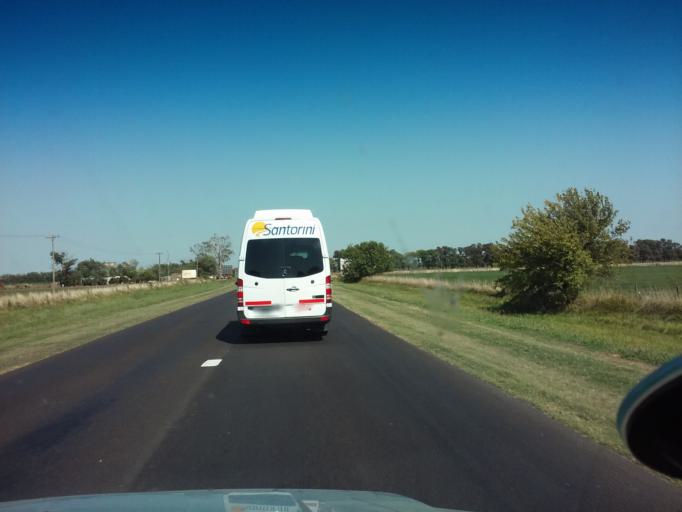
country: AR
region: Buenos Aires
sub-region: Partido de Chivilcoy
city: Chivilcoy
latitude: -34.9589
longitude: -60.0376
